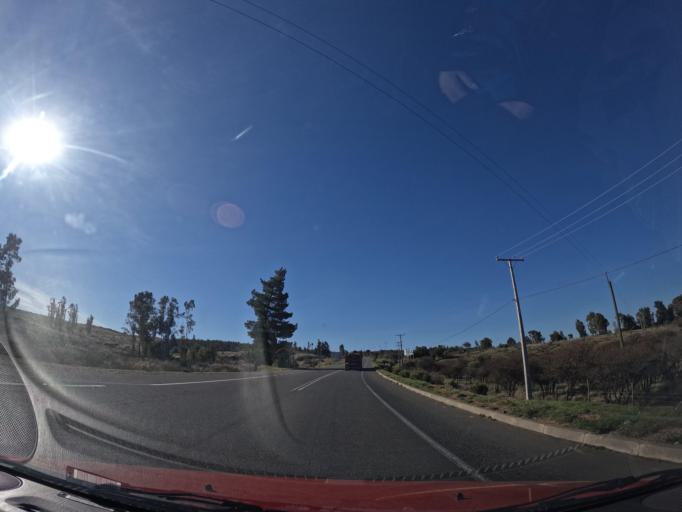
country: CL
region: Maule
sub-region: Provincia de Cauquenes
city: Cauquenes
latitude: -35.9429
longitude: -72.1994
